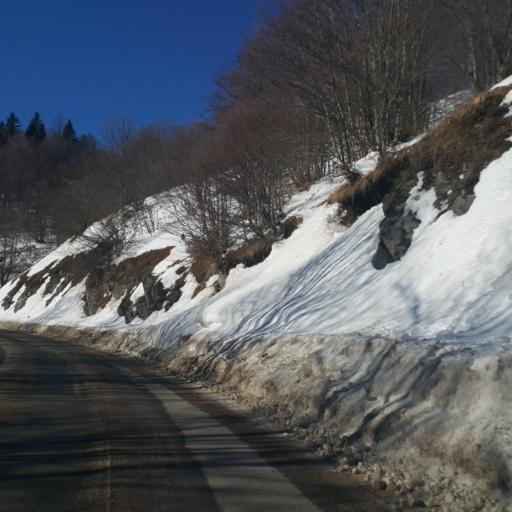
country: XK
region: Mitrovica
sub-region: Komuna e Leposaviqit
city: Leposaviq
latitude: 43.3134
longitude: 20.8516
